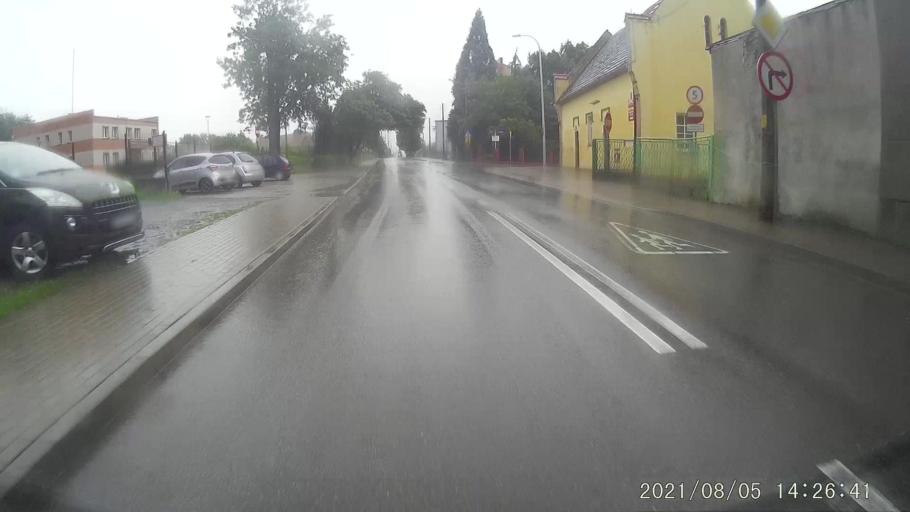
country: PL
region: Opole Voivodeship
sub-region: Powiat nyski
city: Korfantow
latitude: 50.4890
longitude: 17.5986
